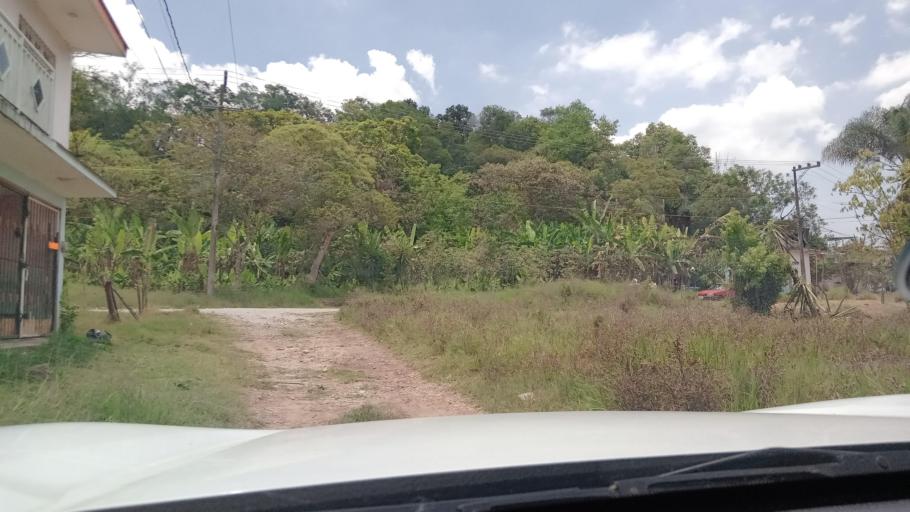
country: MX
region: Veracruz
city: Coatepec
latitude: 19.4319
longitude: -96.9785
